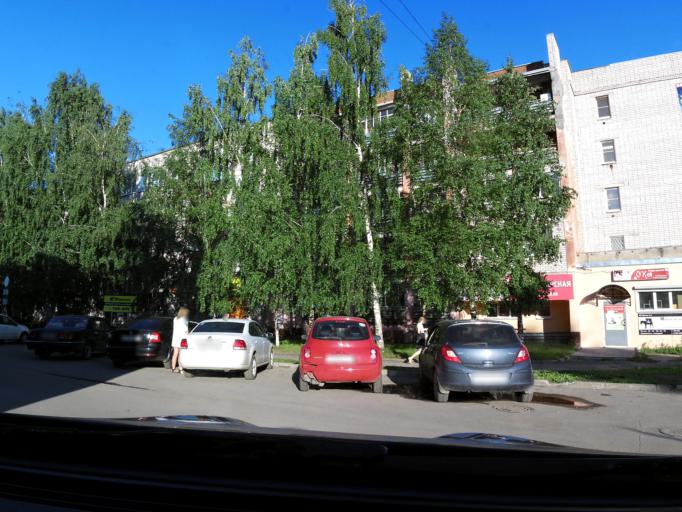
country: RU
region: Vologda
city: Vologda
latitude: 59.2212
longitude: 39.9124
